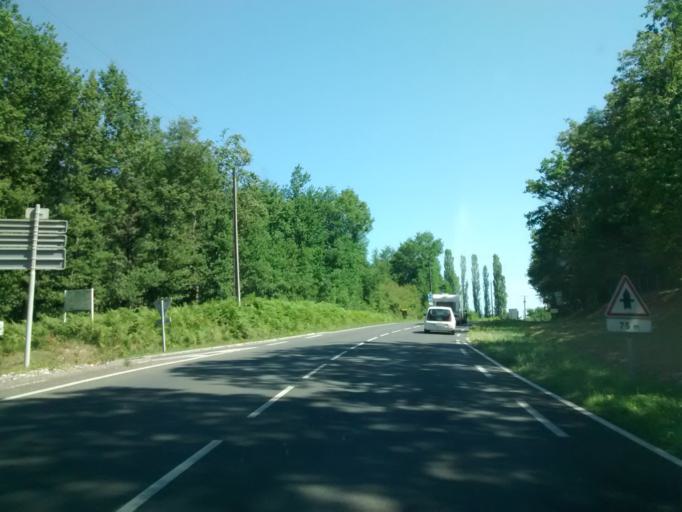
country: FR
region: Aquitaine
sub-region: Departement de la Dordogne
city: Rouffignac-Saint-Cernin-de-Reilhac
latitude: 45.0362
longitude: 0.8971
